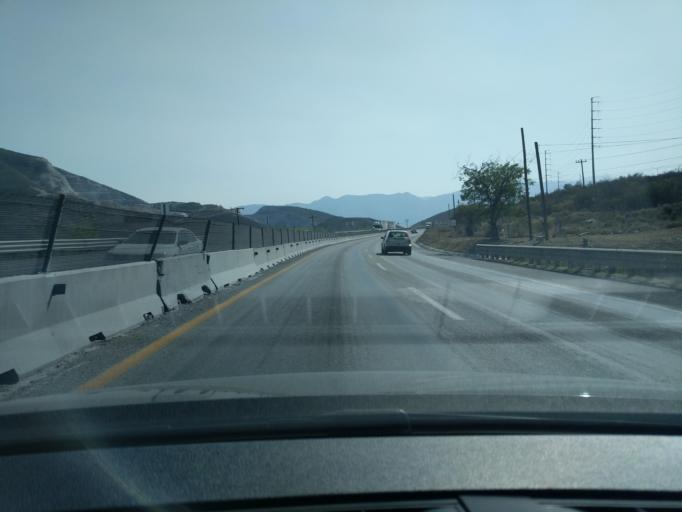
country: MX
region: Nuevo Leon
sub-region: Garcia
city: Los Parques
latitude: 25.7577
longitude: -100.4976
